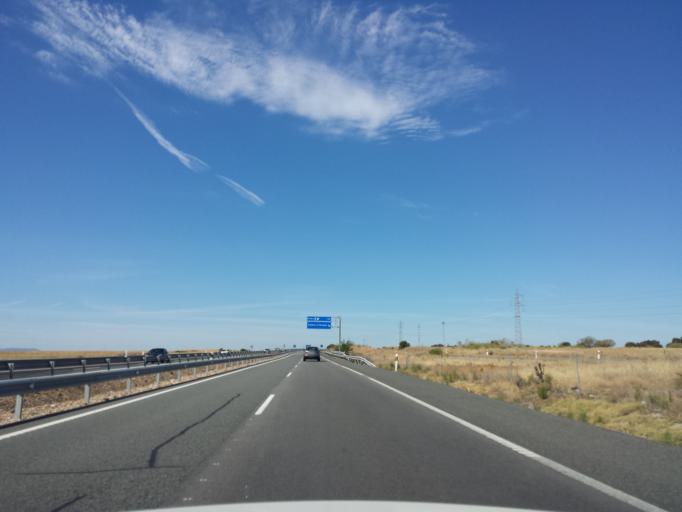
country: ES
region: Castille-La Mancha
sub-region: Province of Toledo
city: Calera y Chozas
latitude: 39.9248
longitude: -5.0285
